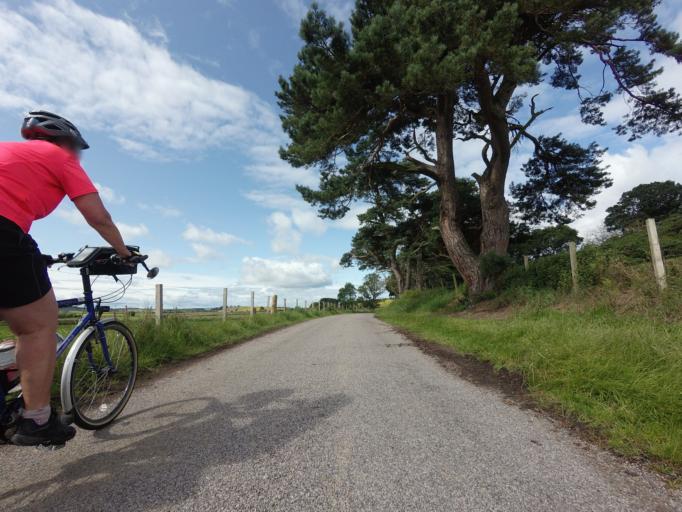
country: GB
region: Scotland
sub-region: Moray
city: Burghead
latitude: 57.6519
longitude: -3.4910
